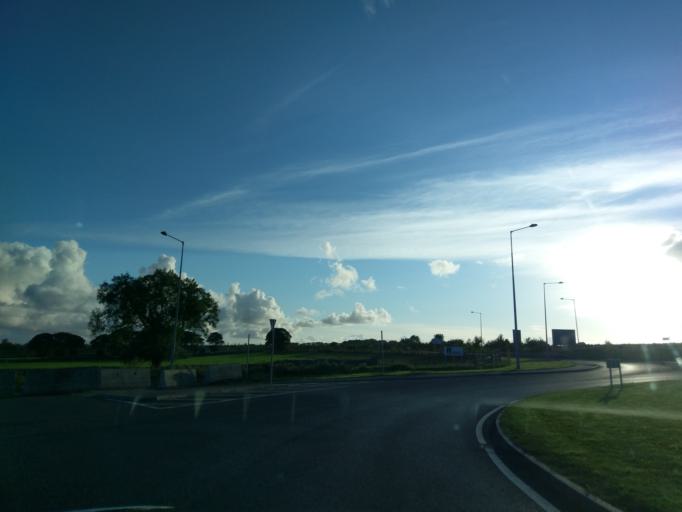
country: IE
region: Connaught
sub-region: County Galway
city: Athenry
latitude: 53.2938
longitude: -8.7614
